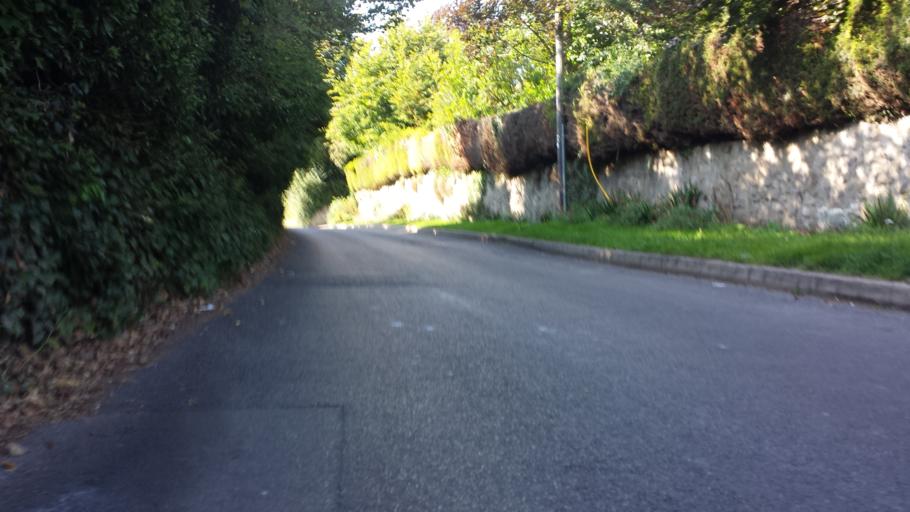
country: GB
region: England
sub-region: Kent
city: Eynsford
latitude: 51.3701
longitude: 0.2082
